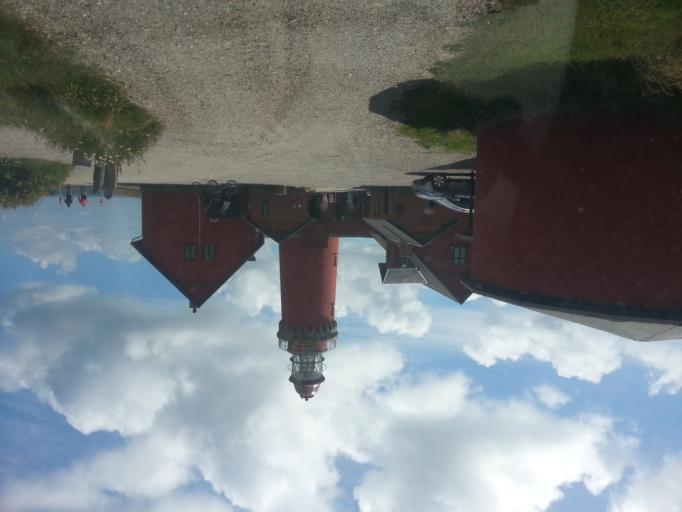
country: DK
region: Central Jutland
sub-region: Lemvig Kommune
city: Harboore
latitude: 56.5133
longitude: 8.1208
